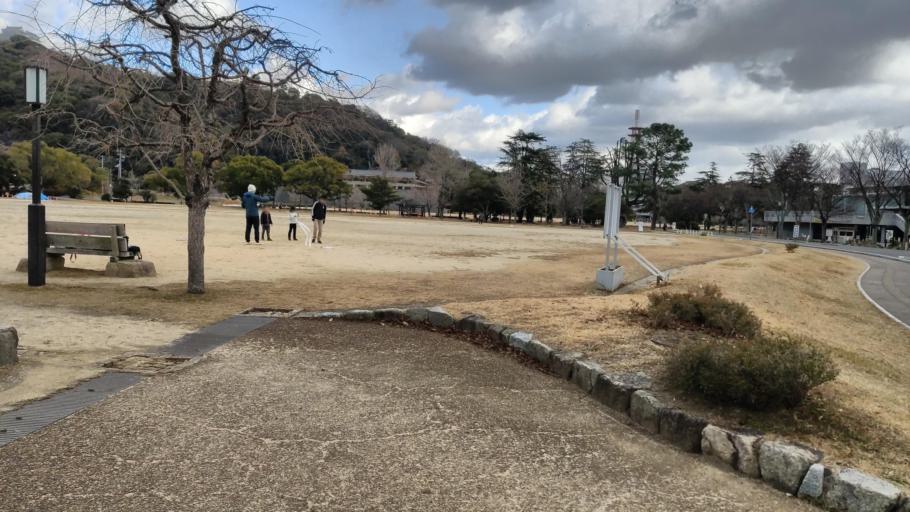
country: JP
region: Ehime
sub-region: Shikoku-chuo Shi
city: Matsuyama
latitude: 33.8418
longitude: 132.7597
